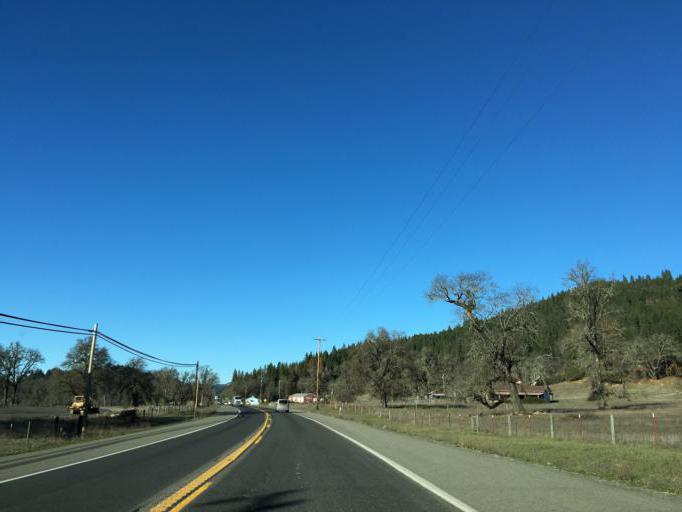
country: US
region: California
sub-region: Mendocino County
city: Laytonville
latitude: 39.6907
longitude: -123.4831
